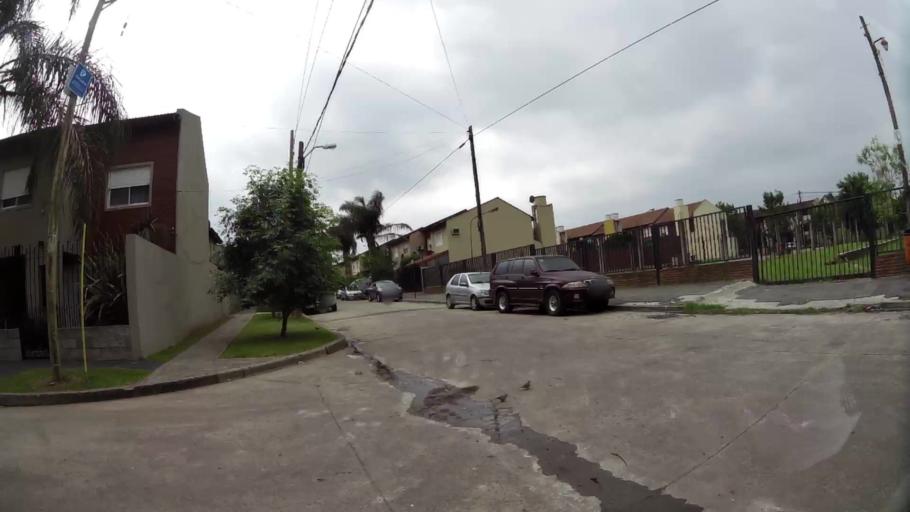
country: AR
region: Buenos Aires
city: San Justo
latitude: -34.7310
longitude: -58.5200
